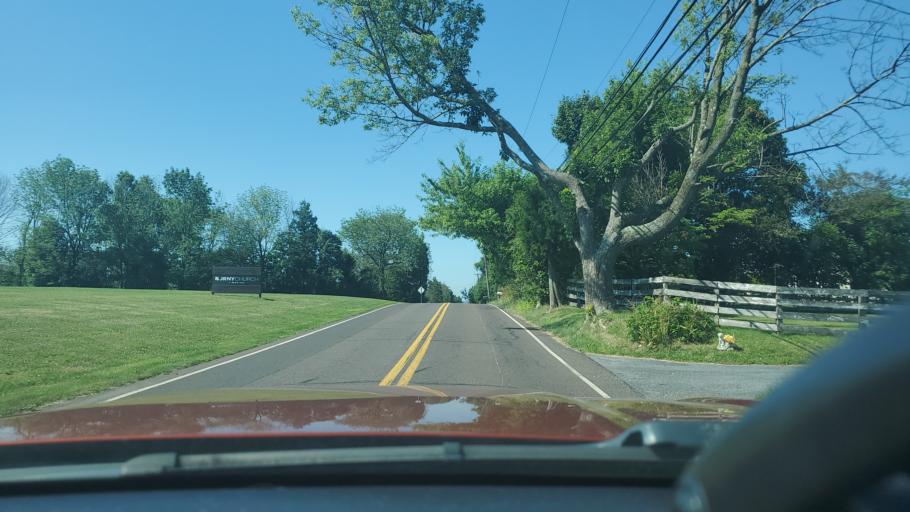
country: US
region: Pennsylvania
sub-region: Montgomery County
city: Limerick
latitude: 40.2579
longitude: -75.5214
